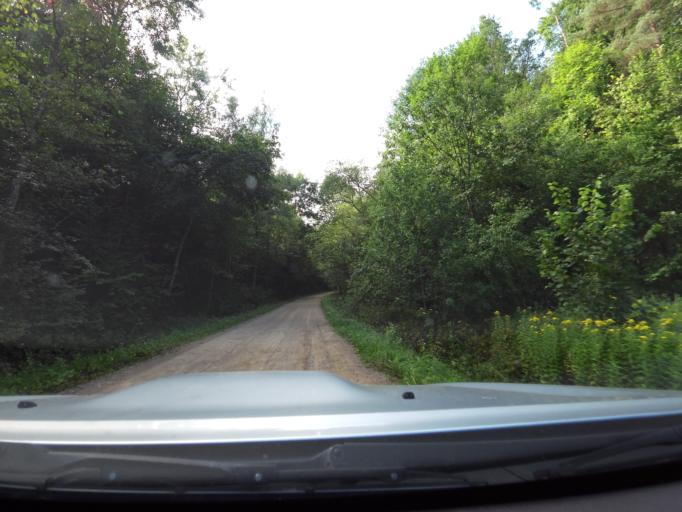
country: LT
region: Vilnius County
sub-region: Vilniaus Rajonas
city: Vievis
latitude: 54.8185
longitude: 24.9681
